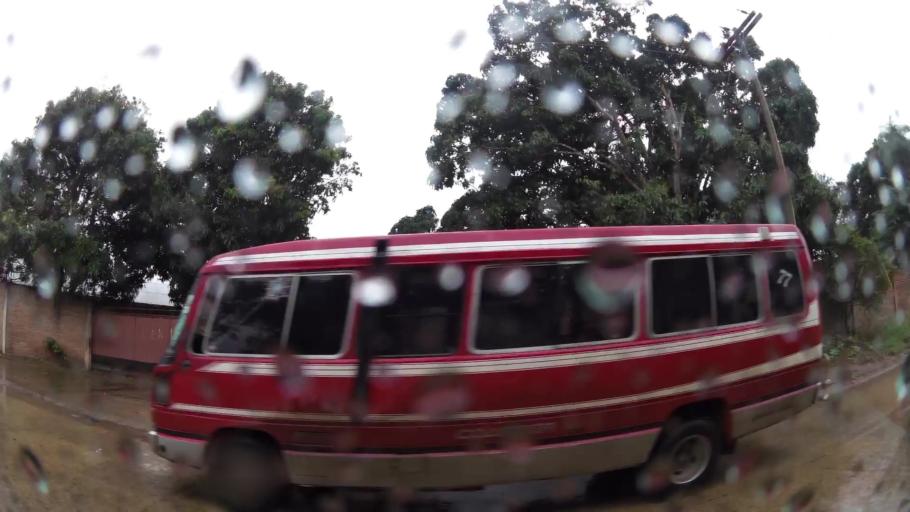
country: BO
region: Santa Cruz
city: Santa Cruz de la Sierra
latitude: -17.8051
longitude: -63.2274
